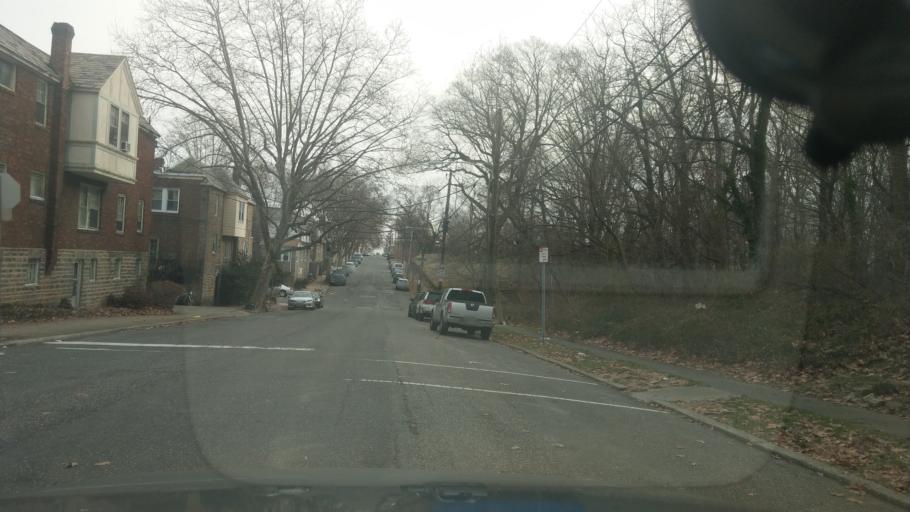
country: US
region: Pennsylvania
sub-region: Montgomery County
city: Jenkintown
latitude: 40.0447
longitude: -75.1333
